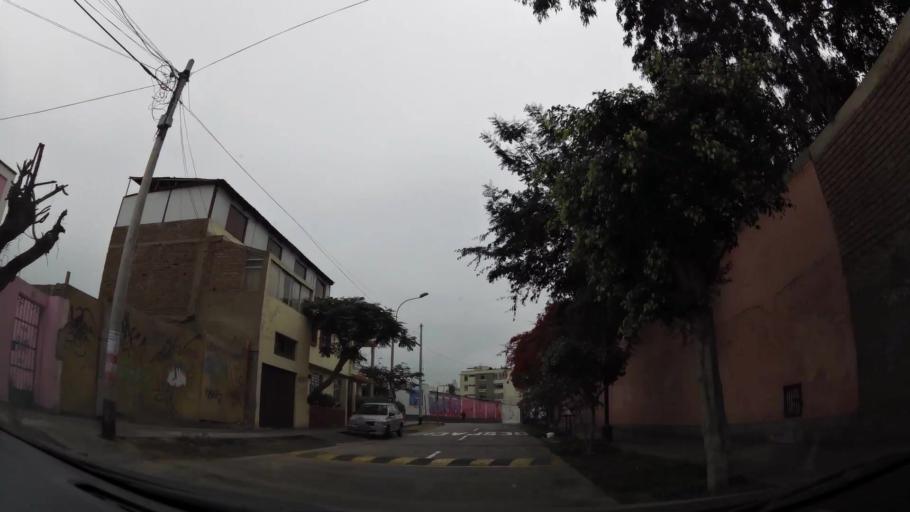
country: PE
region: Lima
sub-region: Lima
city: San Isidro
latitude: -12.0796
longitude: -77.0639
